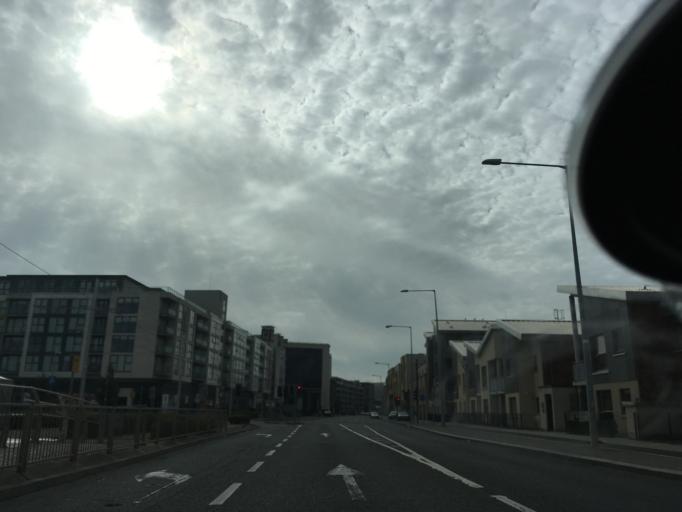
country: IE
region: Leinster
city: Tallaght
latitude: 53.2893
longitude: -6.3790
